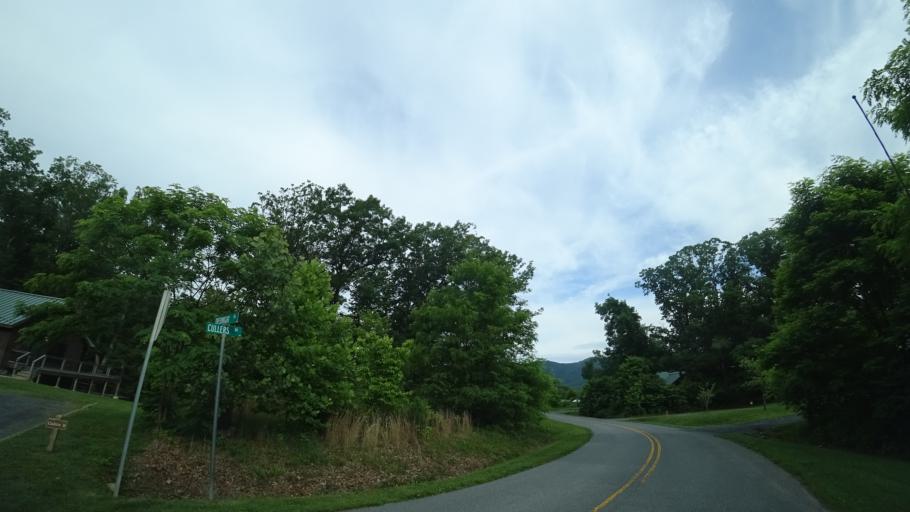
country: US
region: Virginia
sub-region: Warren County
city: Front Royal
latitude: 38.8479
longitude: -78.3168
